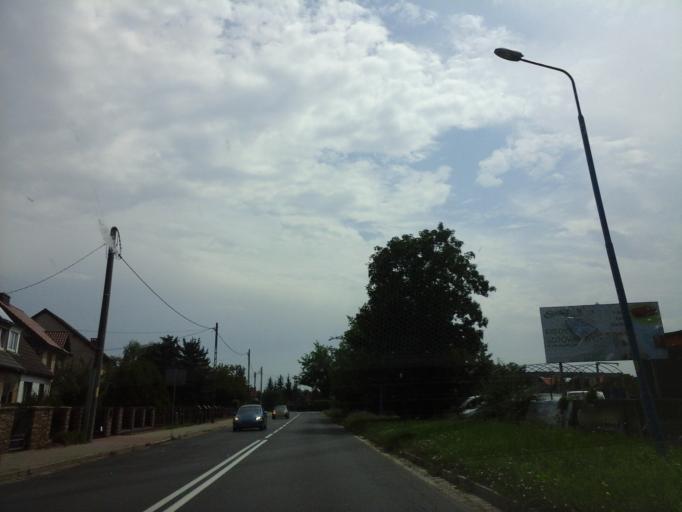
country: PL
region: Lower Silesian Voivodeship
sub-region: Powiat strzelinski
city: Strzelin
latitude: 50.7905
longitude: 17.0663
